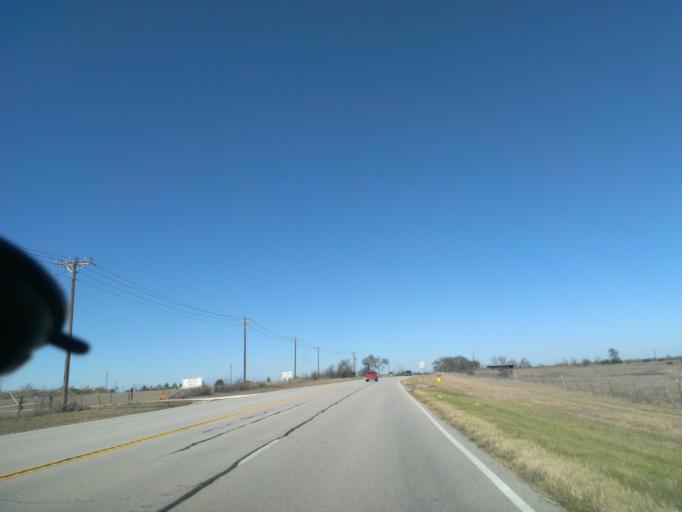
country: US
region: Texas
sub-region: Williamson County
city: Florence
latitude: 30.8408
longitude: -97.9040
